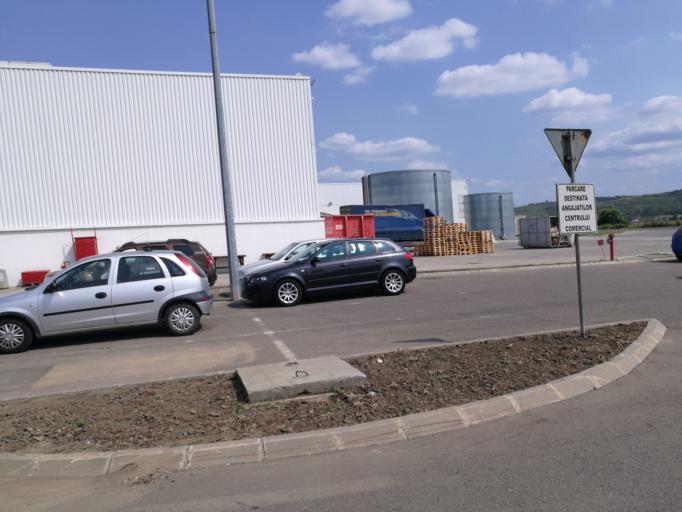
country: RO
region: Iasi
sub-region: Comuna Miroslava
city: Miroslava
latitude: 47.1664
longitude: 27.5115
